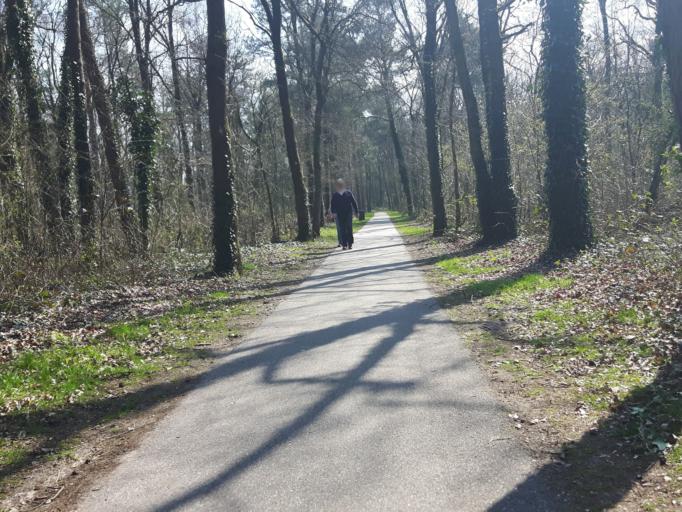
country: NL
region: Overijssel
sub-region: Gemeente Enschede
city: Enschede
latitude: 52.1841
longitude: 6.8446
